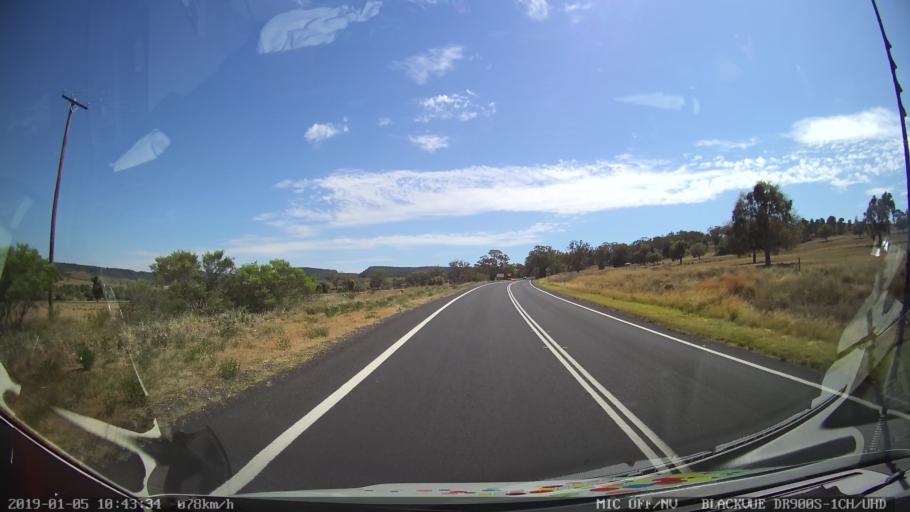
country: AU
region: New South Wales
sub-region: Warrumbungle Shire
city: Coonabarabran
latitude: -31.4633
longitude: 148.9888
